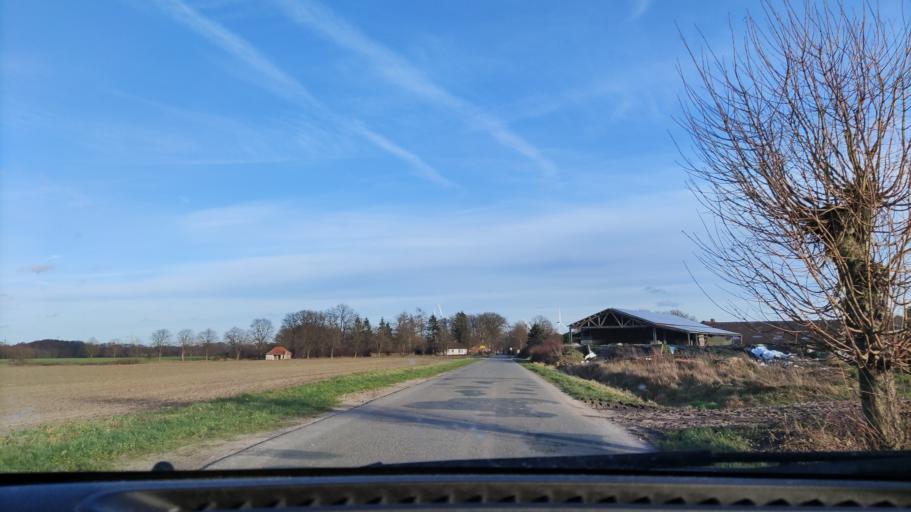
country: DE
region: Lower Saxony
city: Eimke
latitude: 52.9824
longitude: 10.3617
